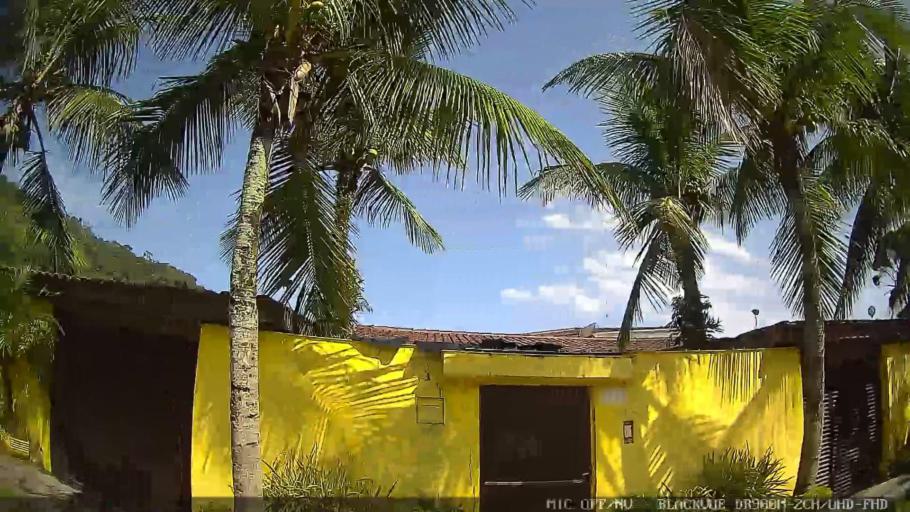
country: BR
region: Sao Paulo
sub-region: Guaruja
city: Guaruja
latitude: -23.9786
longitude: -46.1926
